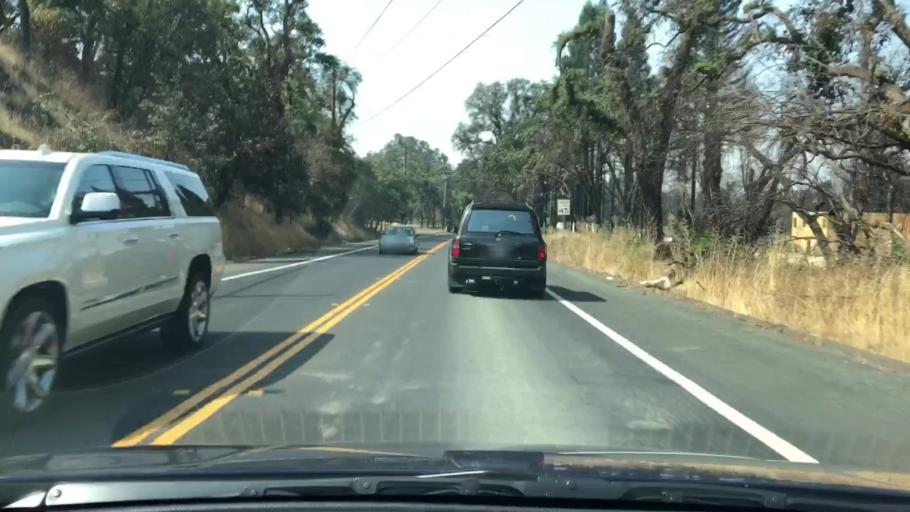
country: US
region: California
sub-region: Sonoma County
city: Larkfield-Wikiup
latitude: 38.5042
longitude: -122.7343
